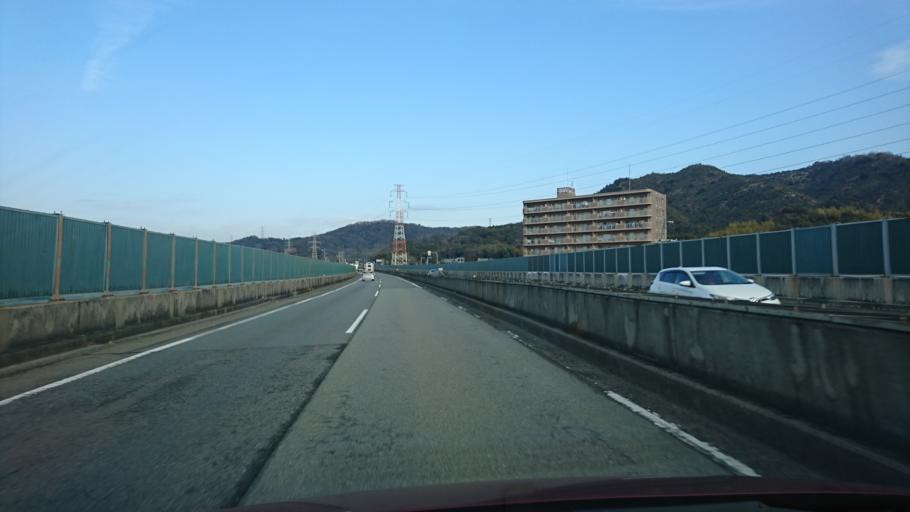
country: JP
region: Hyogo
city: Himeji
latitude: 34.8402
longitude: 134.7379
